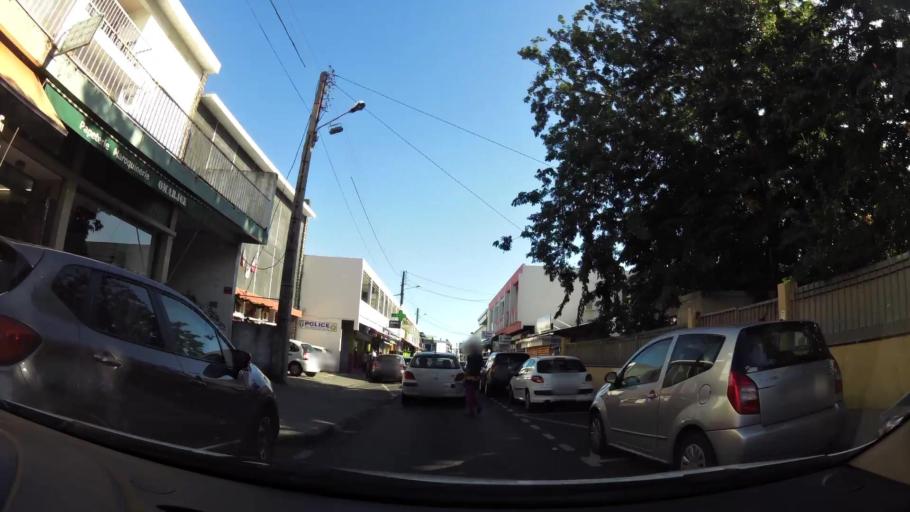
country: RE
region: Reunion
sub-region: Reunion
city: Saint-Louis
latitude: -21.2859
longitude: 55.4088
